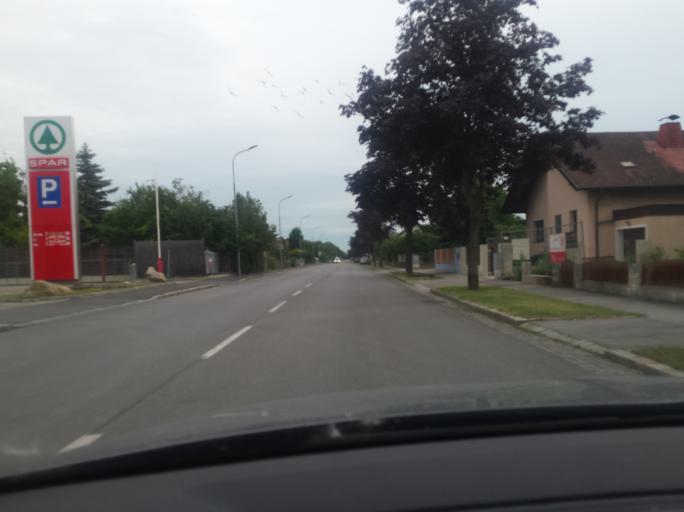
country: AT
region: Lower Austria
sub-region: Politischer Bezirk Ganserndorf
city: Deutsch-Wagram
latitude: 48.3156
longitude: 16.5765
